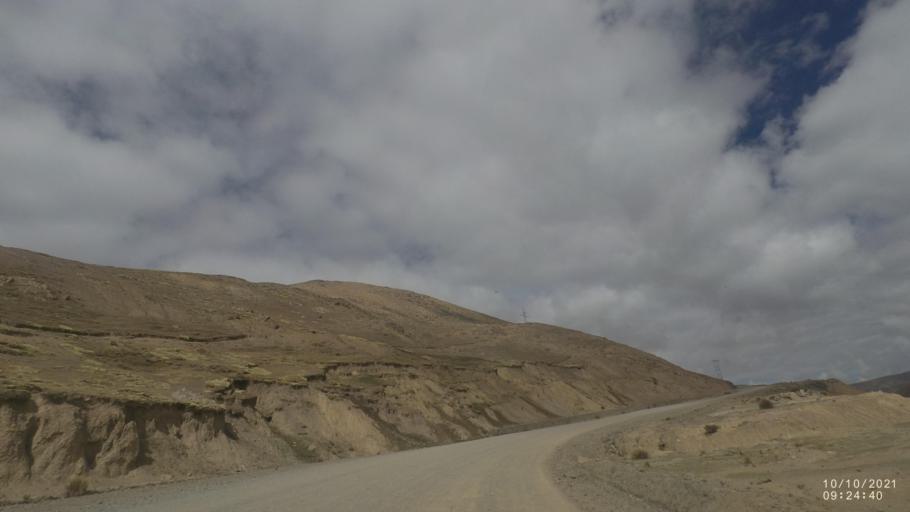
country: BO
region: La Paz
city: Quime
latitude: -17.0912
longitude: -67.3103
